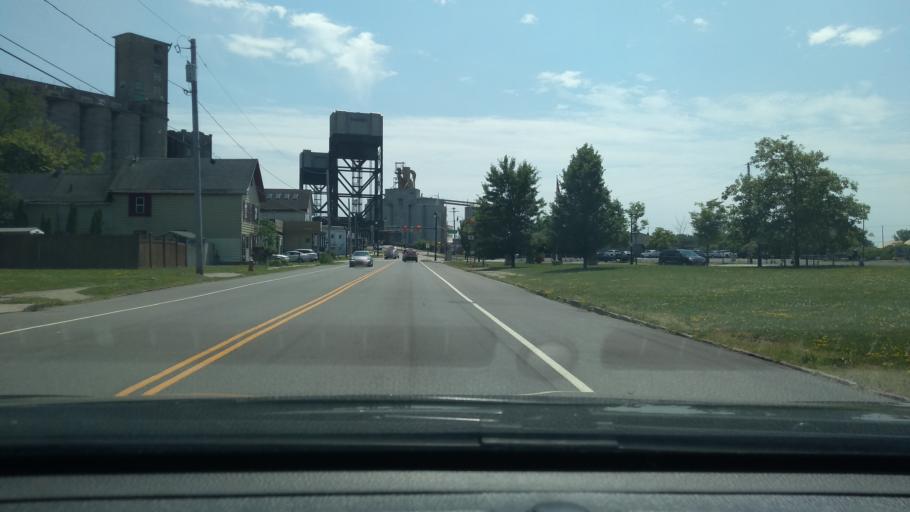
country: US
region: New York
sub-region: Erie County
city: Buffalo
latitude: 42.8644
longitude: -78.8670
